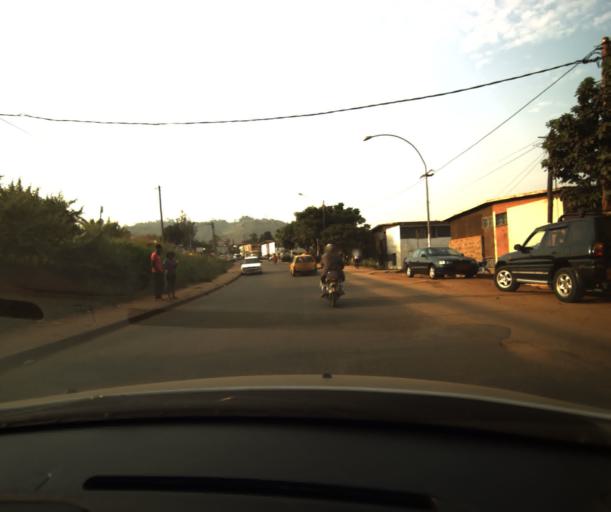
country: CM
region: Centre
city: Yaounde
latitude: 3.8761
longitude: 11.4921
